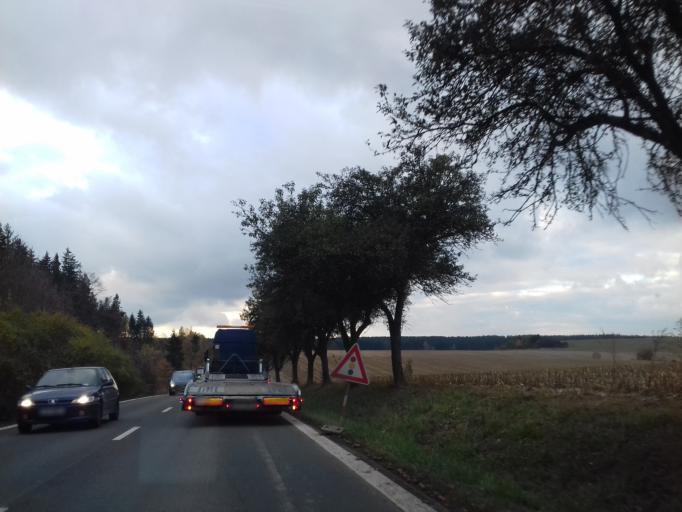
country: CZ
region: Pardubicky
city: Pomezi
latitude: 49.7321
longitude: 16.3407
